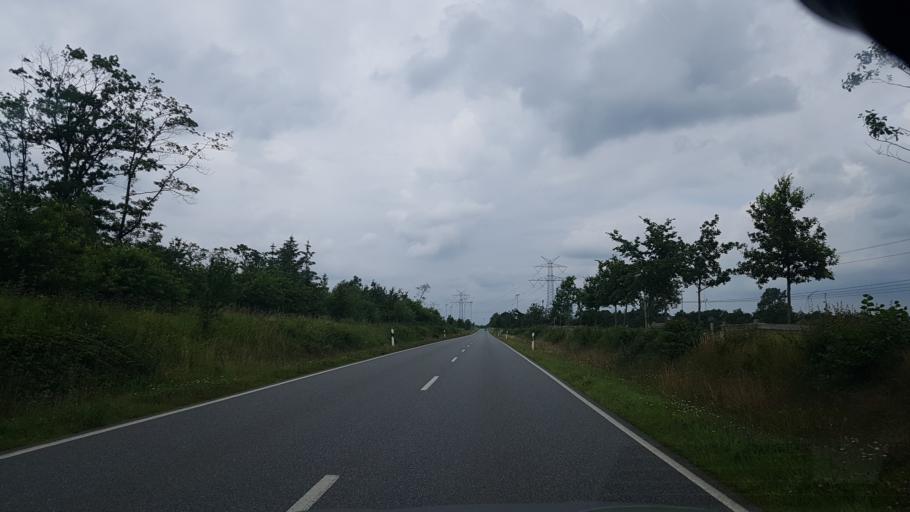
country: DE
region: Schleswig-Holstein
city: Jardelund
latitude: 54.8254
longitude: 9.2196
